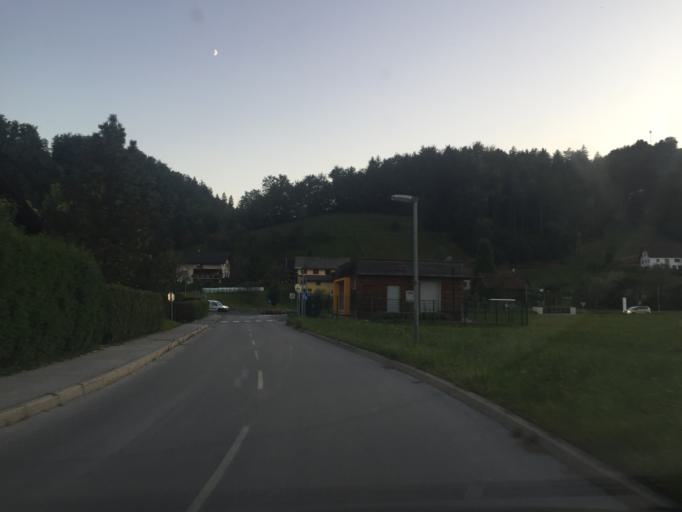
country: SI
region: Sostanj
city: Sostanj
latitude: 46.3831
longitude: 15.0299
